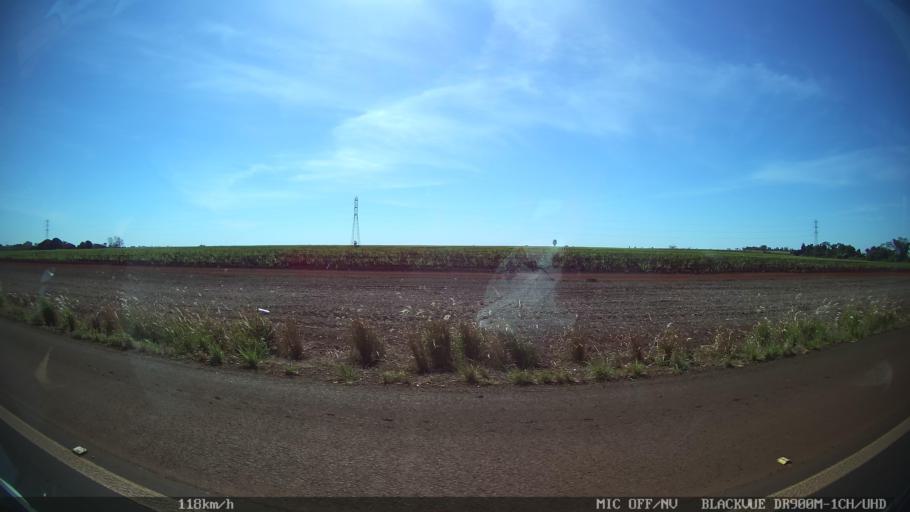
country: BR
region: Sao Paulo
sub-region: Guaira
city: Guaira
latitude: -20.4455
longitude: -48.4037
